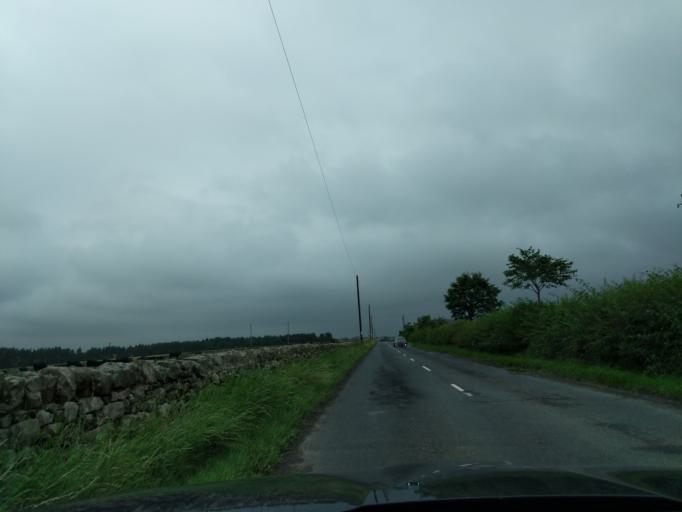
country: GB
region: England
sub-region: Northumberland
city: Ford
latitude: 55.6592
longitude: -2.1078
